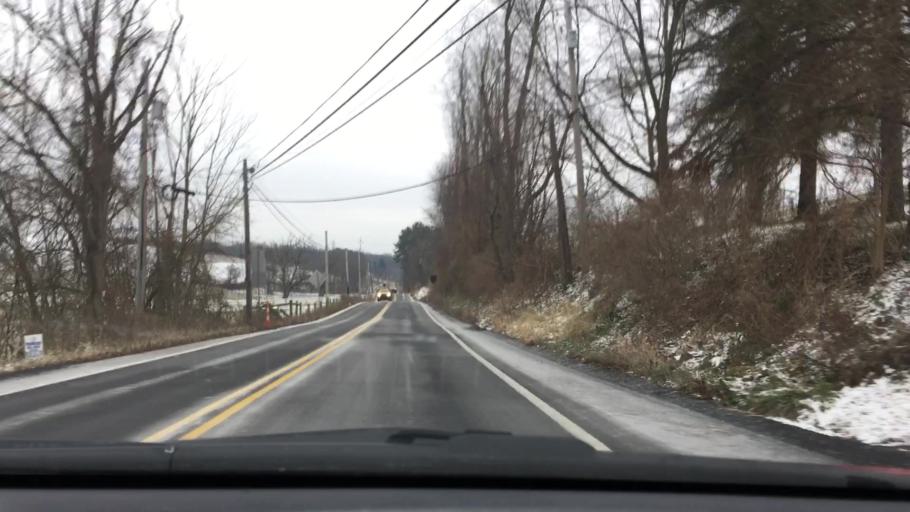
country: US
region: Pennsylvania
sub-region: Allegheny County
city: Enlow
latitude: 40.4349
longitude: -80.2077
